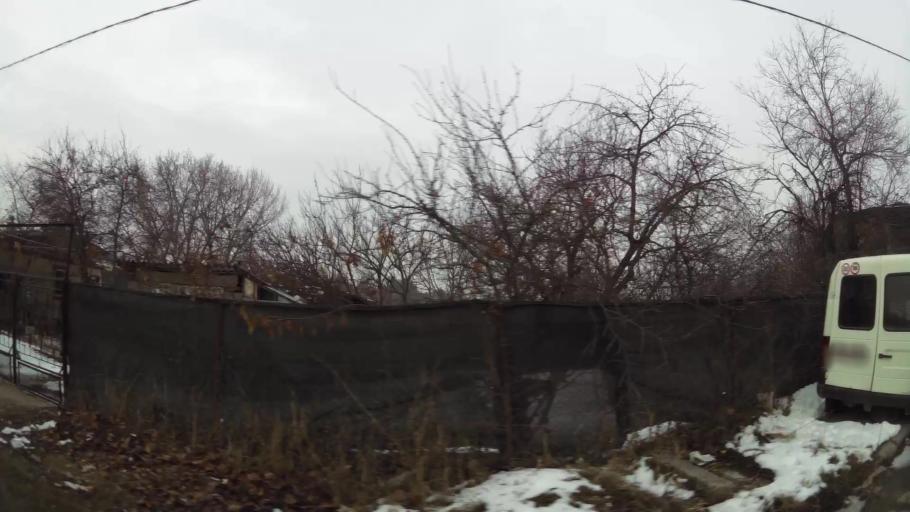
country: MK
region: Suto Orizari
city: Suto Orizare
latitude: 42.0442
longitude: 21.4292
